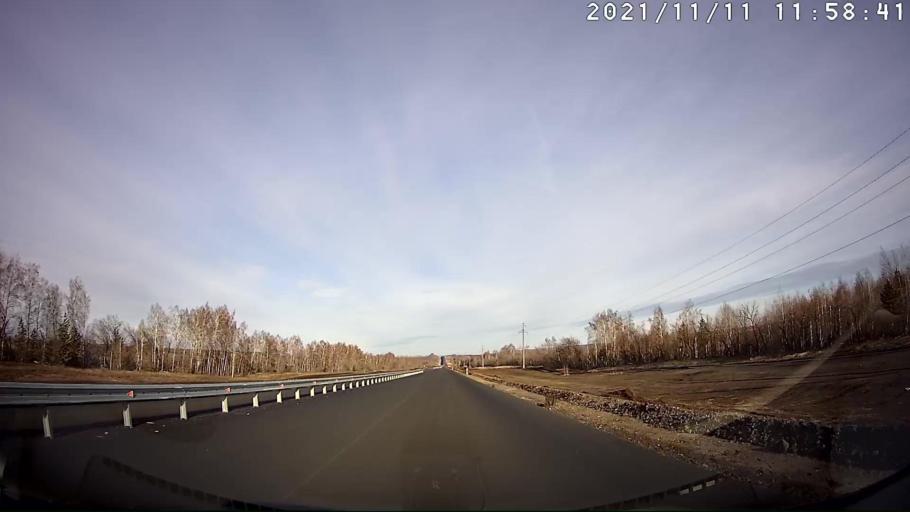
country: RU
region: Samara
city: Balasheyka
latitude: 53.5838
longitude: 48.3331
